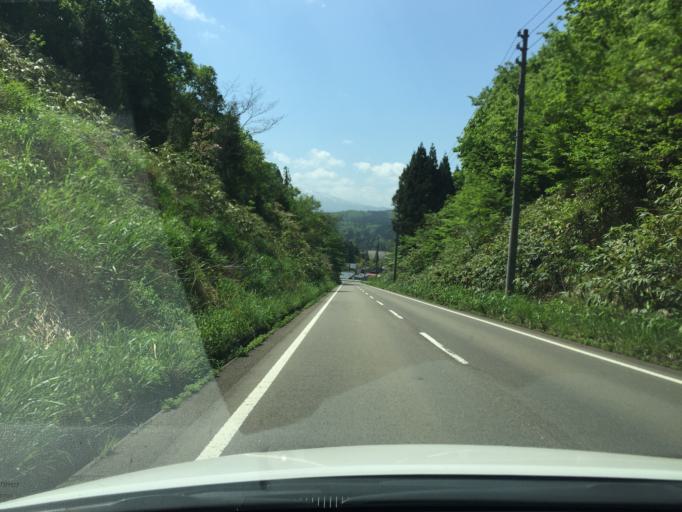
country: JP
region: Niigata
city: Kamo
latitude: 37.5572
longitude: 139.0778
